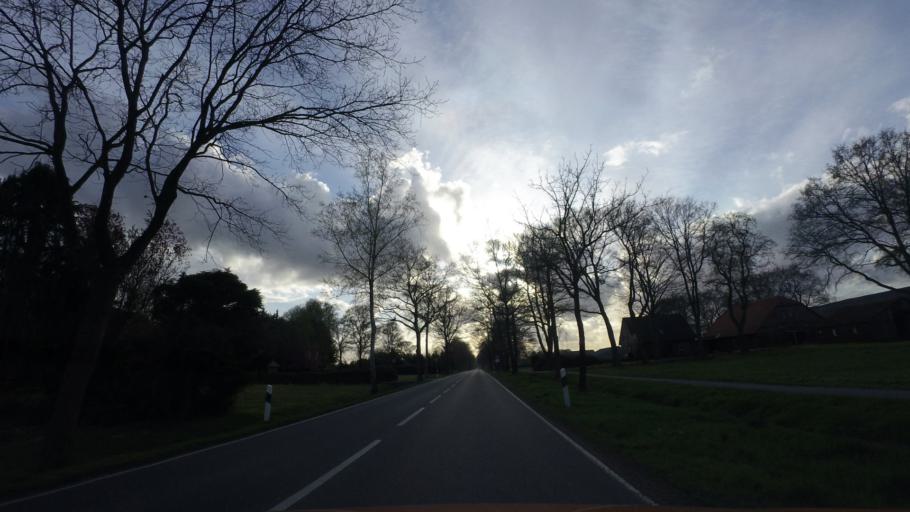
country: DE
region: Lower Saxony
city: Edewecht
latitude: 53.1237
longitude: 8.0680
